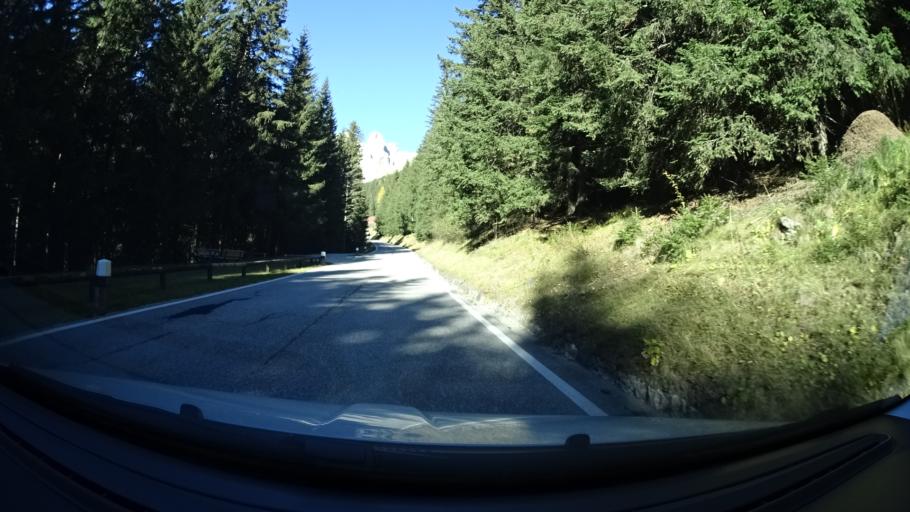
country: IT
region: Trentino-Alto Adige
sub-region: Provincia di Trento
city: Canazei
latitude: 46.4833
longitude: 11.7809
